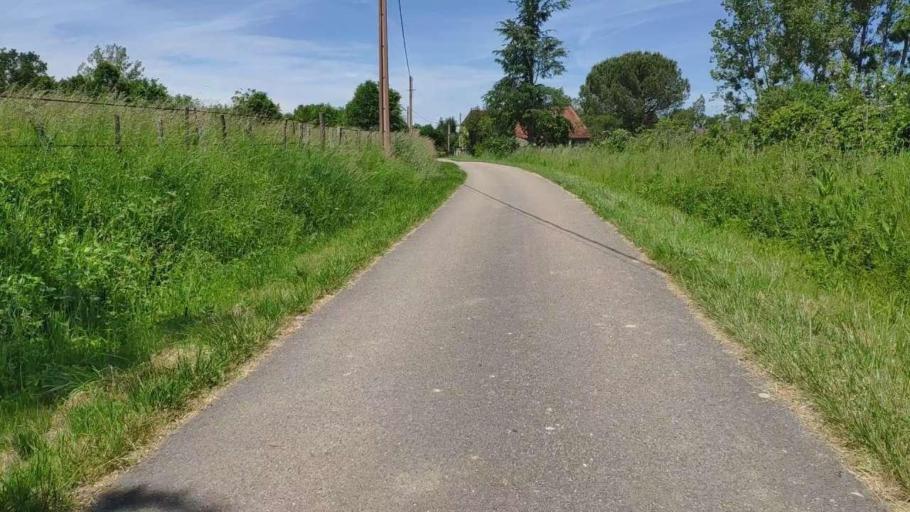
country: FR
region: Franche-Comte
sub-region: Departement du Jura
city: Bletterans
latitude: 46.8010
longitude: 5.3885
